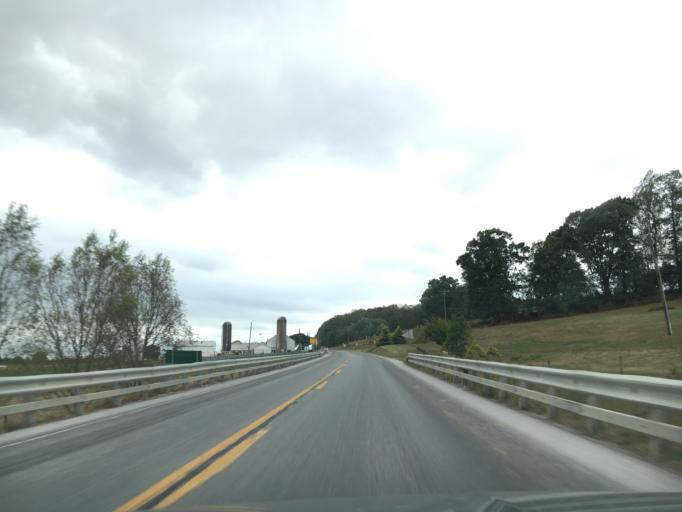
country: US
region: Pennsylvania
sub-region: Lancaster County
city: Quarryville
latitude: 39.9077
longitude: -76.1230
